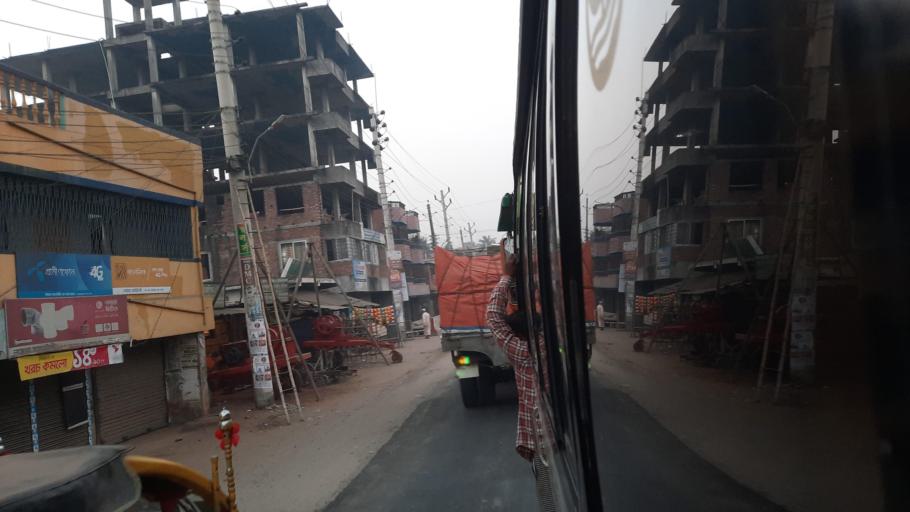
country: BD
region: Khulna
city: Jessore
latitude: 23.1717
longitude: 89.1925
